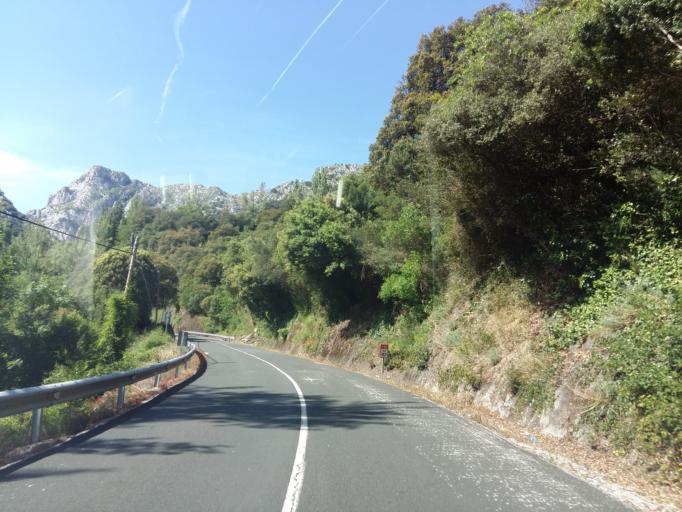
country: ES
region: Cantabria
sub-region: Provincia de Cantabria
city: Potes
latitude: 43.2174
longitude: -4.5918
